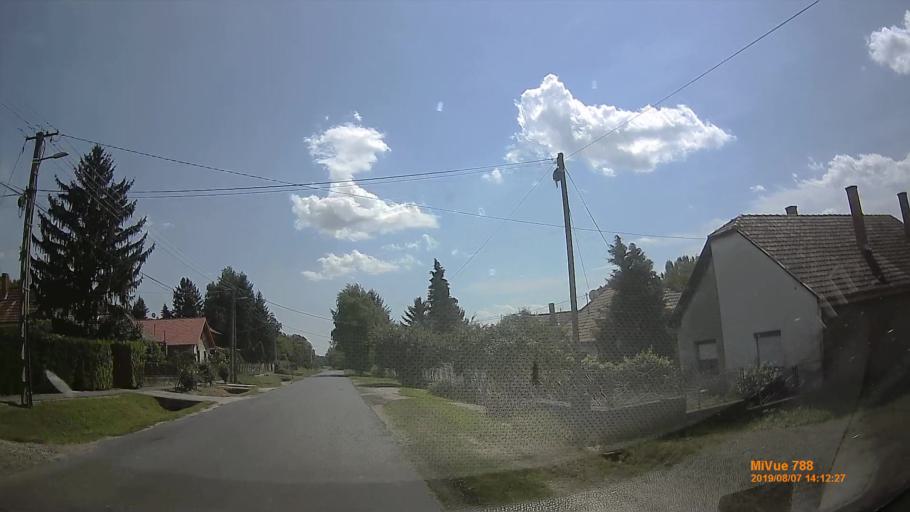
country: HU
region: Zala
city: Heviz
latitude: 46.8311
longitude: 17.1180
